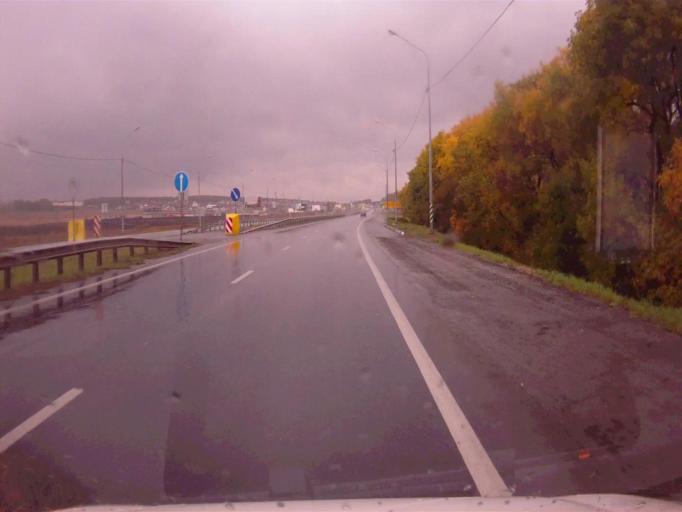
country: RU
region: Chelyabinsk
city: Dolgoderevenskoye
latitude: 55.2700
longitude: 61.3446
